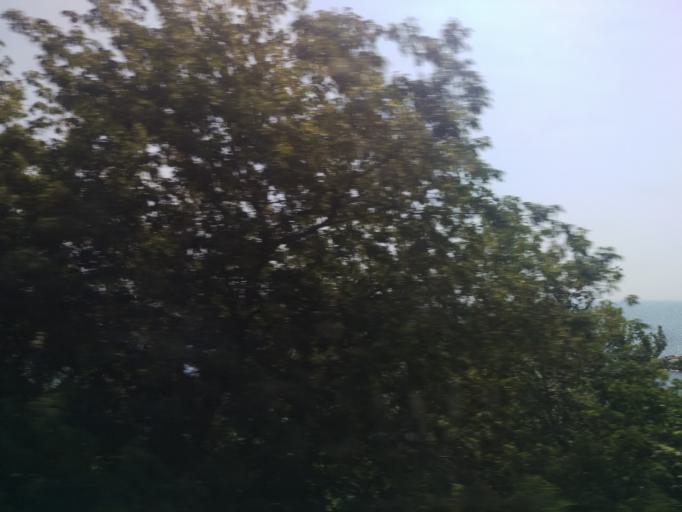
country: CA
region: Ontario
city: Scarborough
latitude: 43.7725
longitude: -79.1374
